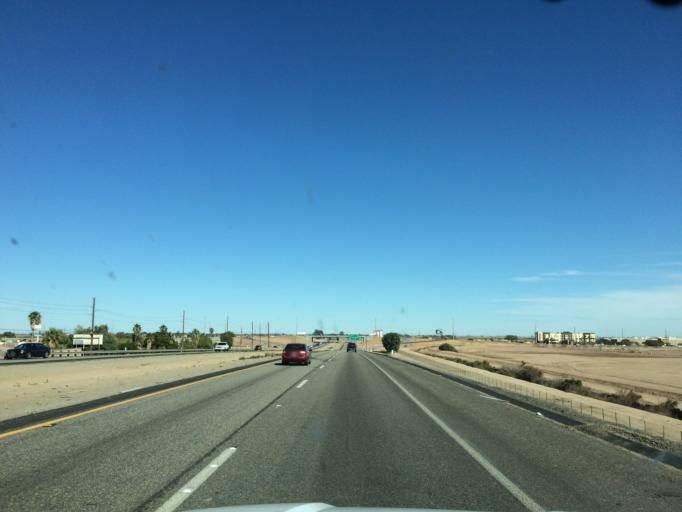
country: US
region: California
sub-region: Imperial County
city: El Centro
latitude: 32.7736
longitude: -115.5427
